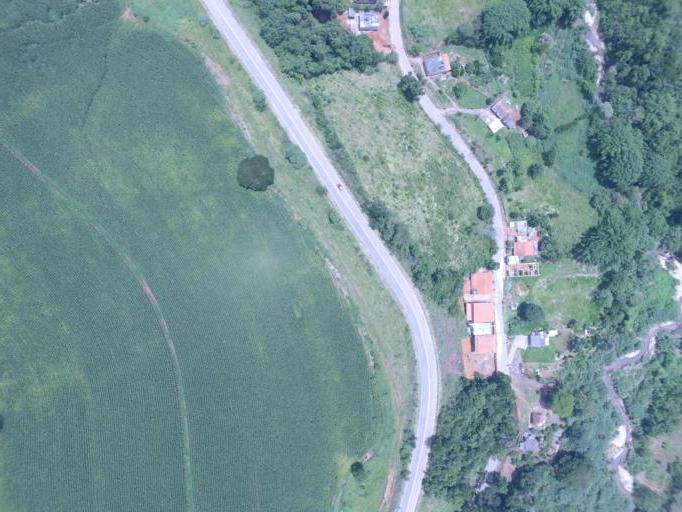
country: BR
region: Minas Gerais
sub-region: Tiradentes
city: Tiradentes
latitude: -21.0881
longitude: -44.0740
